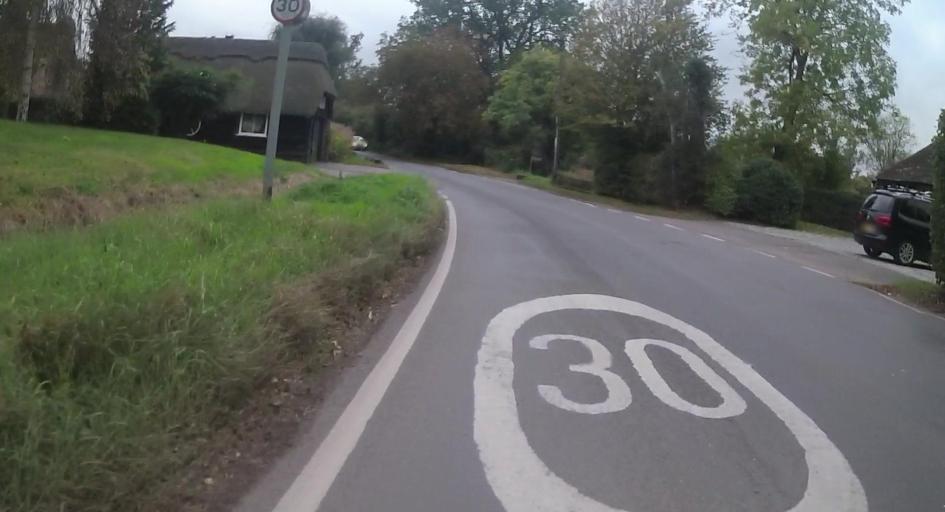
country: GB
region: England
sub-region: Hampshire
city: Fleet
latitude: 51.2647
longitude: -0.8671
